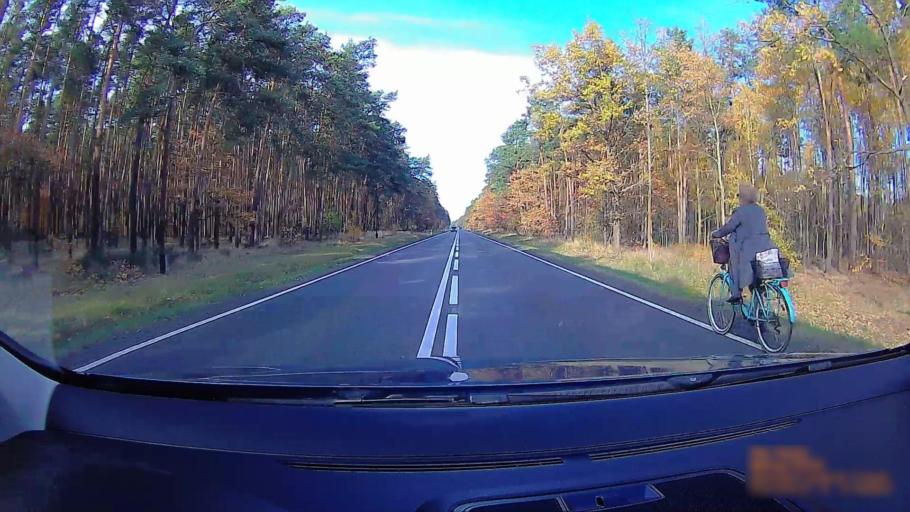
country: PL
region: Greater Poland Voivodeship
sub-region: Powiat ostrzeszowski
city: Ostrzeszow
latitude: 51.4503
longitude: 17.9080
